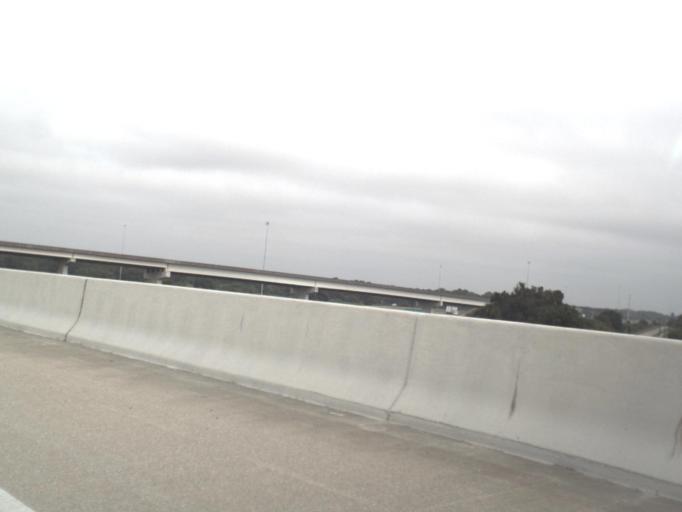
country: US
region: Florida
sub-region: Manatee County
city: Ellenton
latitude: 27.5833
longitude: -82.5145
